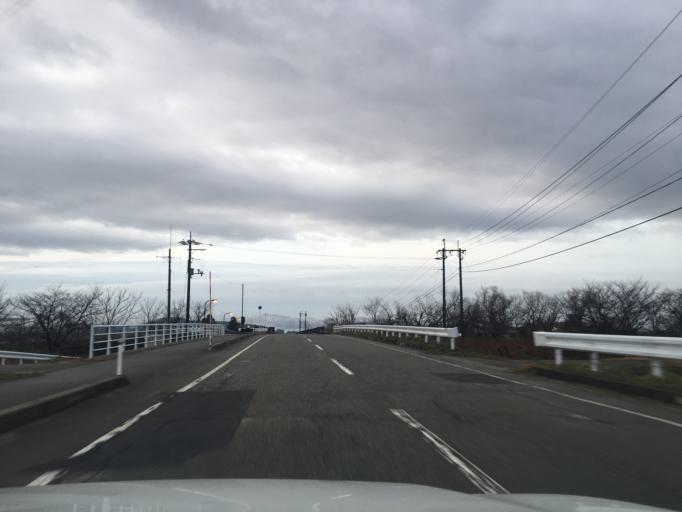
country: JP
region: Niigata
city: Murakami
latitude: 38.2731
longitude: 139.5277
